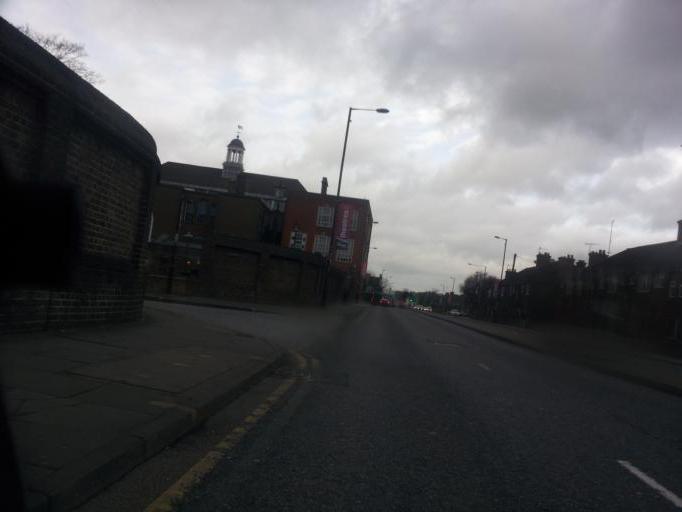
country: GB
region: England
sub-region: Medway
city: Rochester
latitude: 51.3866
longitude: 0.5081
